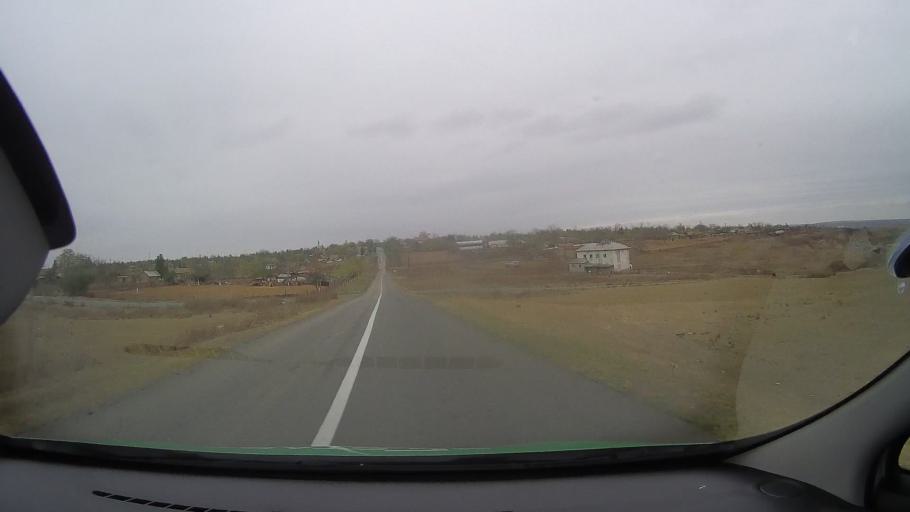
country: RO
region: Constanta
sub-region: Comuna Pantelimon
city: Pantelimon
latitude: 44.5400
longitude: 28.3292
